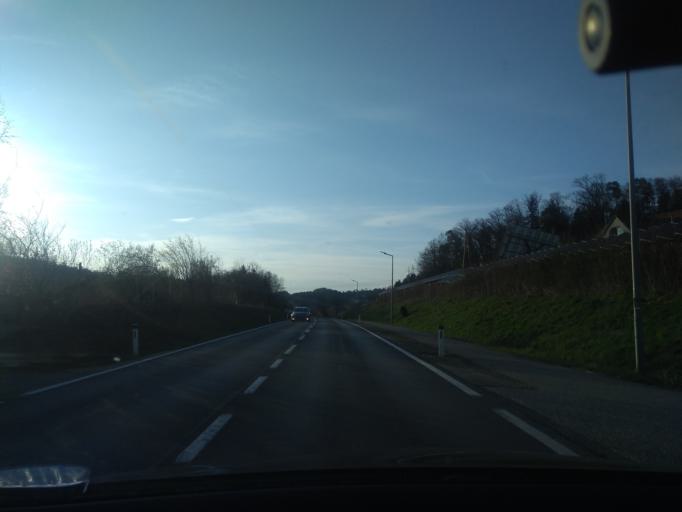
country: AT
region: Styria
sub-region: Politischer Bezirk Leibnitz
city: Heiligenkreuz am Waasen
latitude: 46.9761
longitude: 15.5786
